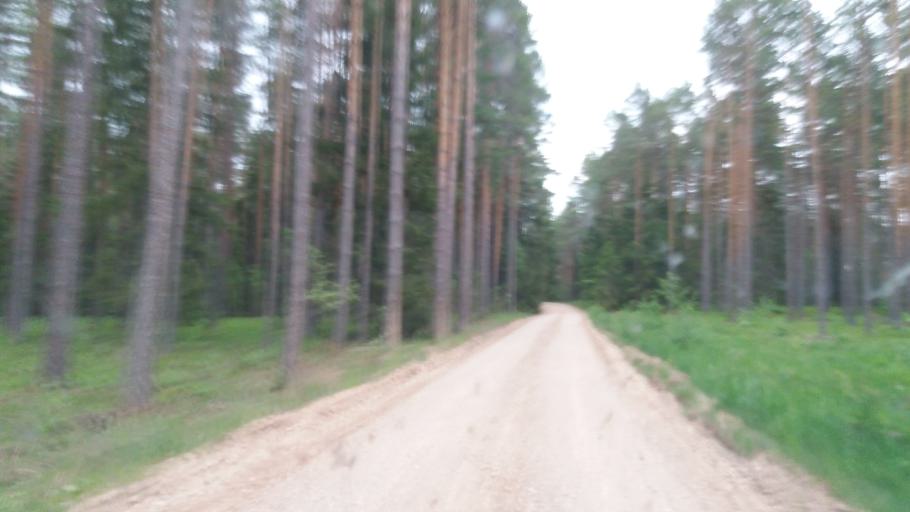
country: LV
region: Kuldigas Rajons
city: Kuldiga
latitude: 57.1572
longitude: 22.1155
